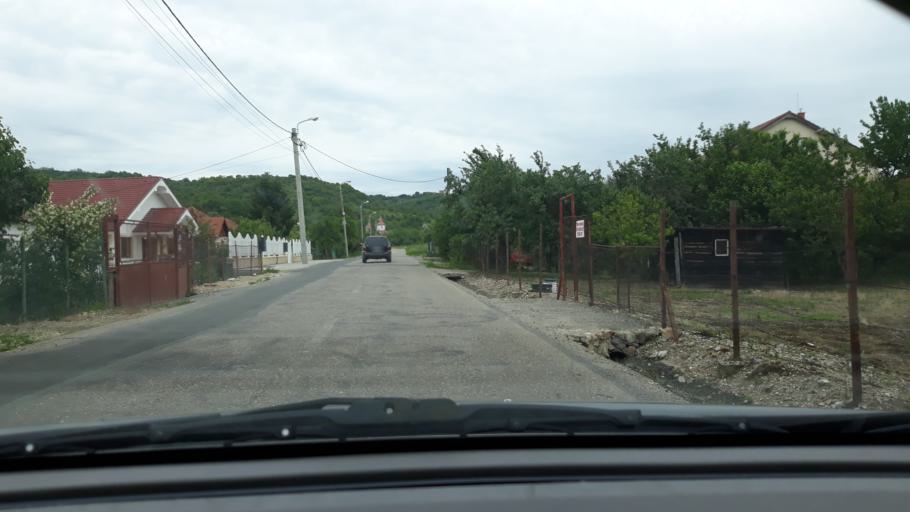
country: RO
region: Bihor
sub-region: Comuna Osorheiu
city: Alparea
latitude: 47.0547
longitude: 22.0012
